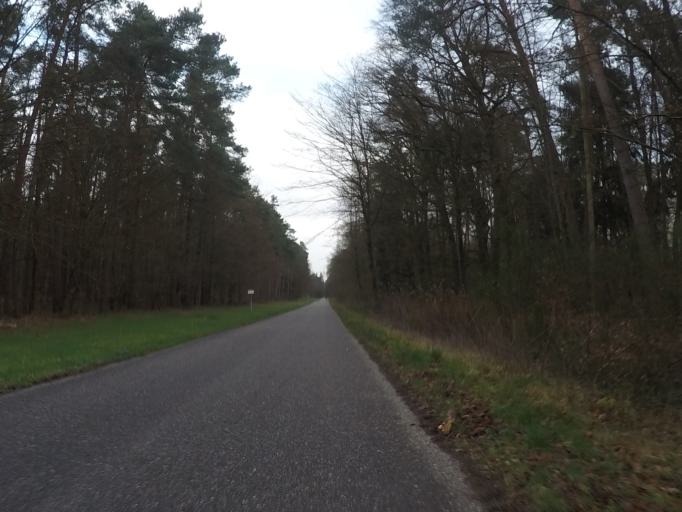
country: DE
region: Rheinland-Pfalz
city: Worth am Rhein
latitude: 49.0553
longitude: 8.2375
